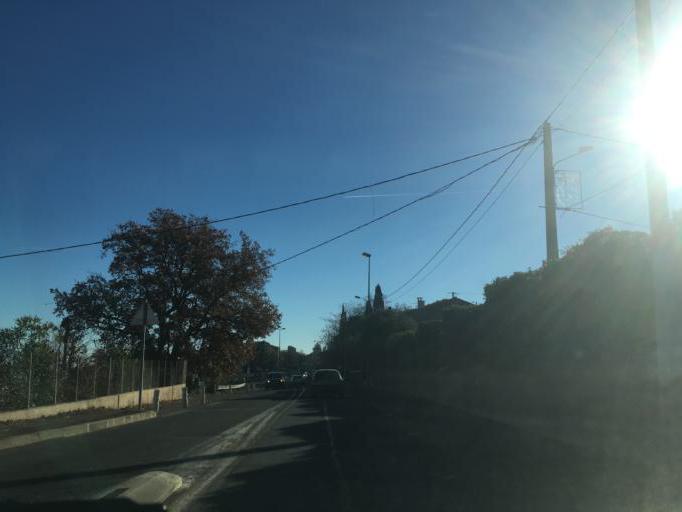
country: FR
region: Provence-Alpes-Cote d'Azur
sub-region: Departement du Var
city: Flayosc
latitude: 43.5364
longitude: 6.3900
